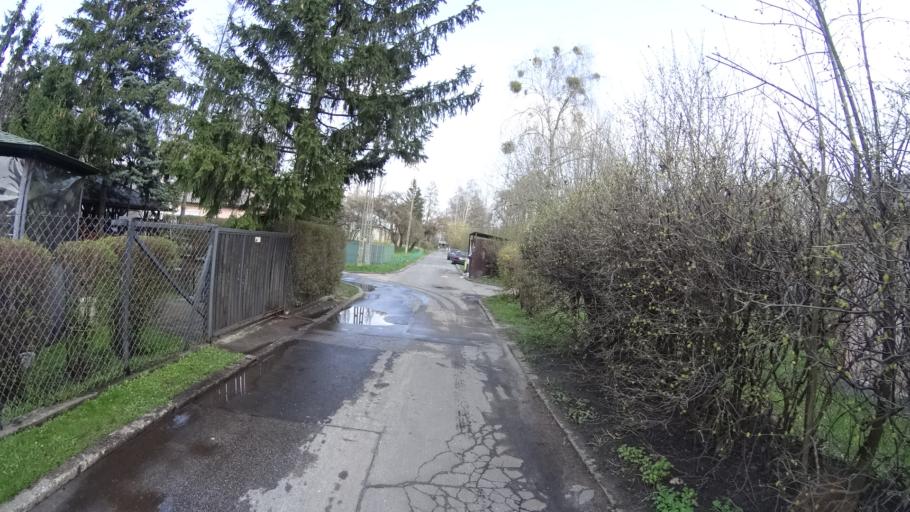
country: PL
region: Masovian Voivodeship
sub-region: Warszawa
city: Bemowo
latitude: 52.2388
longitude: 20.9188
